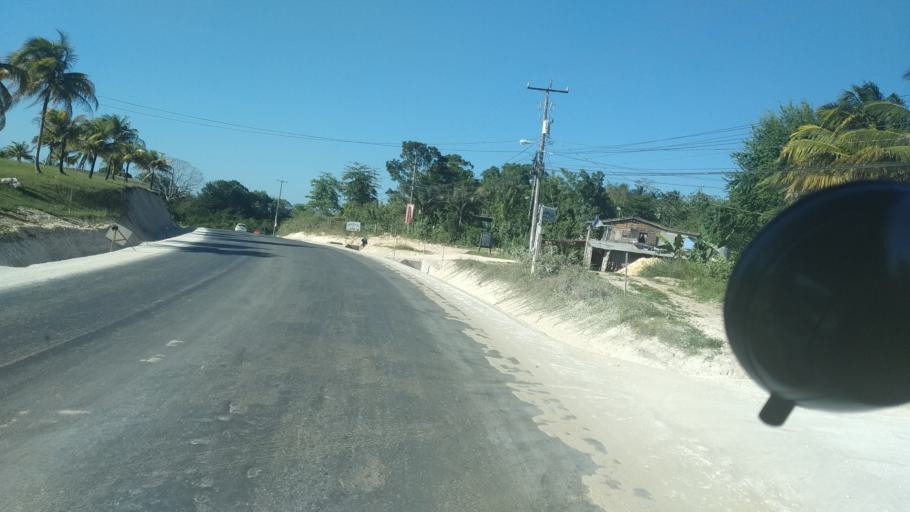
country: BZ
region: Cayo
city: Valley of Peace
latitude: 17.2172
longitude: -88.9333
